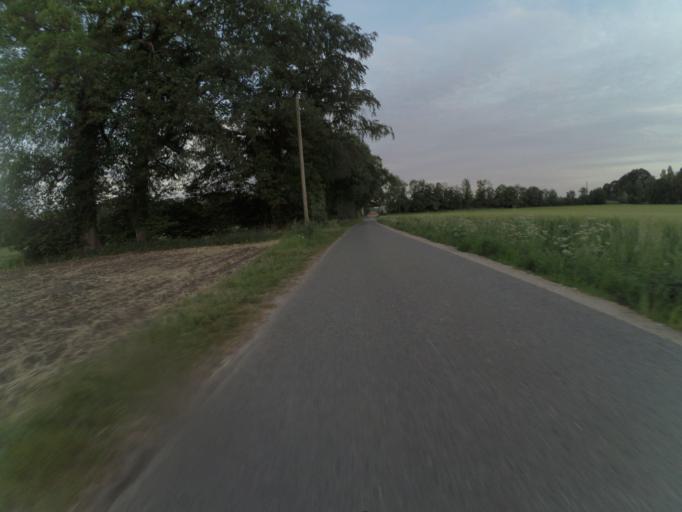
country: DE
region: North Rhine-Westphalia
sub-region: Regierungsbezirk Munster
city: Tecklenburg
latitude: 52.2548
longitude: 7.8105
